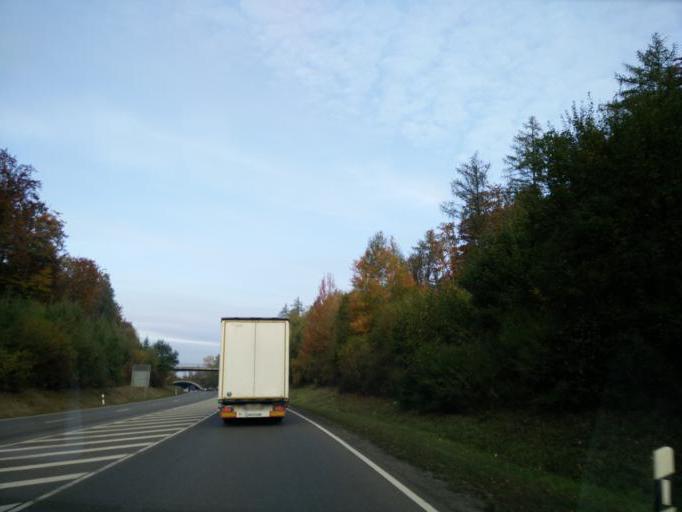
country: DE
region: Baden-Wuerttemberg
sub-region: Regierungsbezirk Stuttgart
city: Holzgerlingen
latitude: 48.6585
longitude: 9.0063
